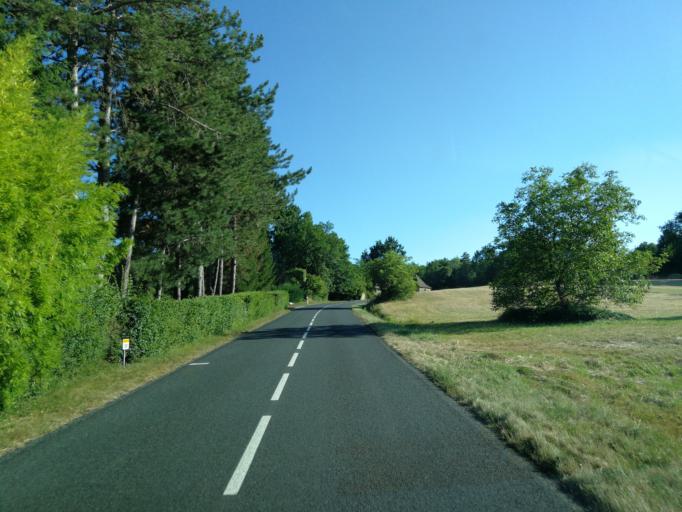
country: FR
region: Midi-Pyrenees
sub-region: Departement du Lot
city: Salviac
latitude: 44.6244
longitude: 1.2166
